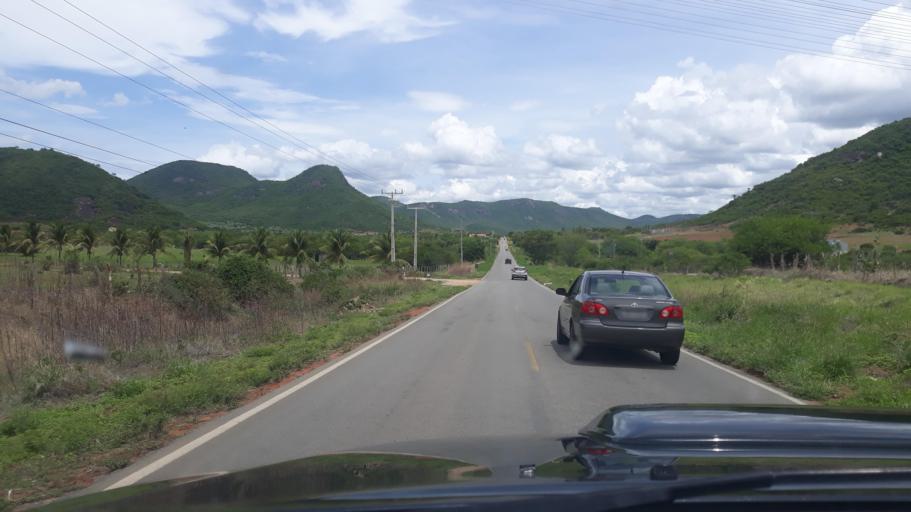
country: BR
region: Bahia
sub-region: Guanambi
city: Guanambi
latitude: -14.2636
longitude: -42.7203
